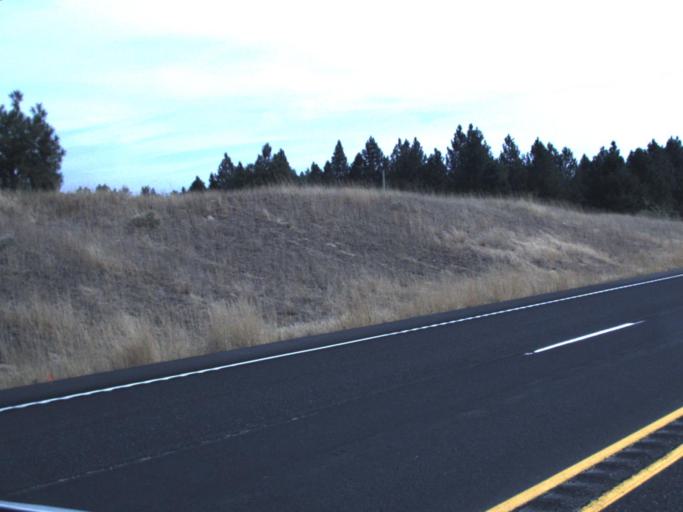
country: US
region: Washington
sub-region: Spokane County
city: Deer Park
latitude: 47.8992
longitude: -117.4356
